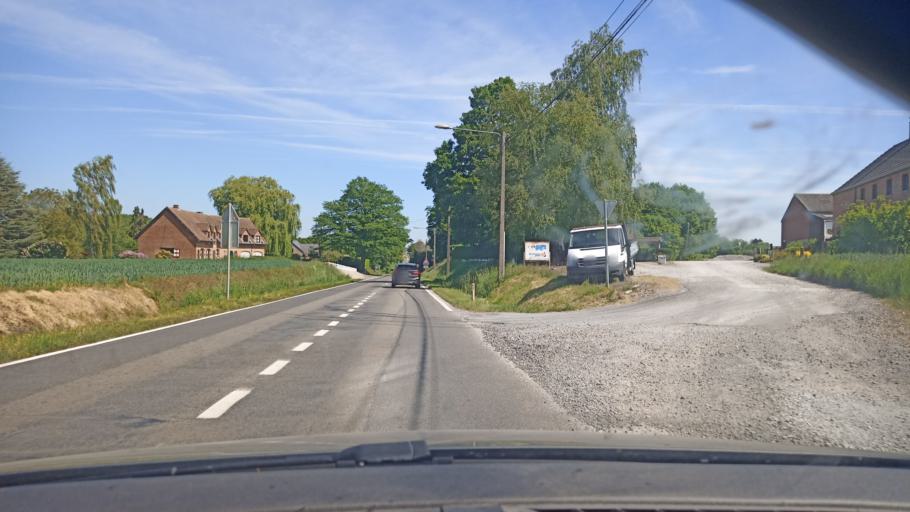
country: BE
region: Wallonia
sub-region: Province du Hainaut
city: Lobbes
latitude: 50.3293
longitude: 4.2622
